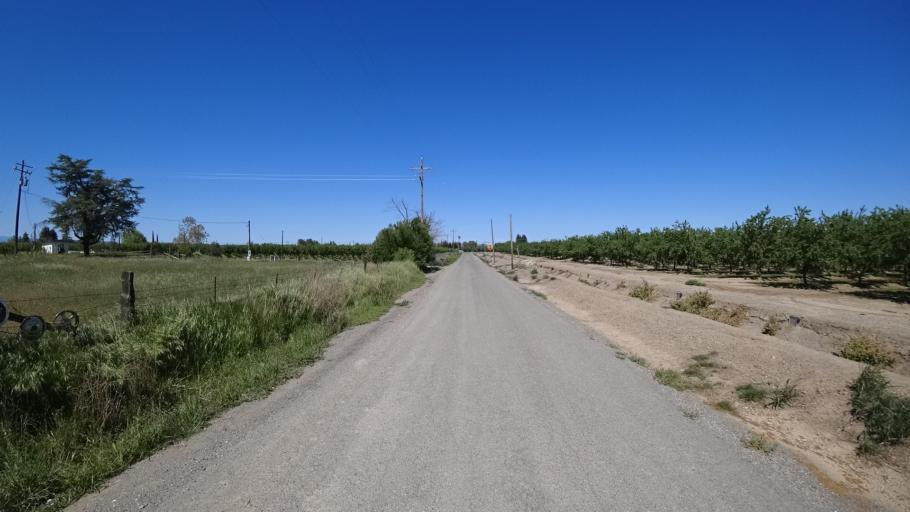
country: US
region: California
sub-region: Glenn County
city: Orland
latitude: 39.7447
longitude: -122.1503
